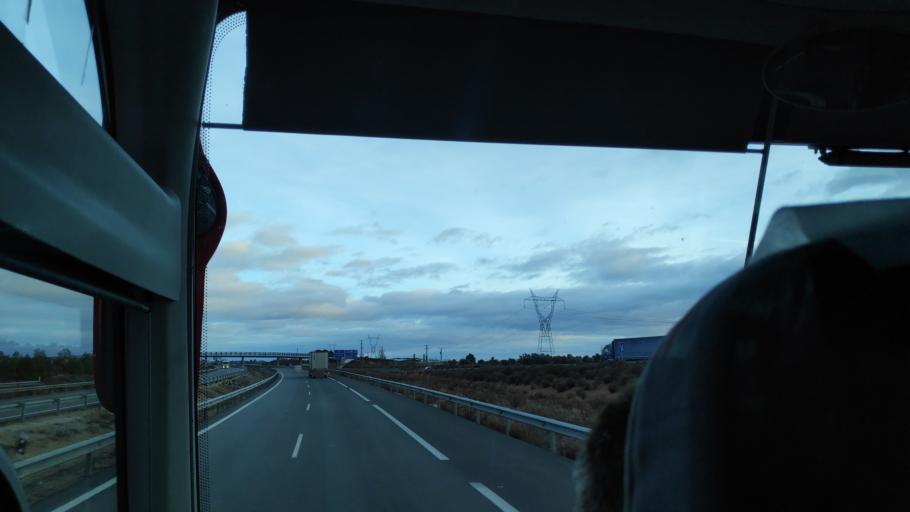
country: ES
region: Castille-La Mancha
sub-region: Provincia de Cuenca
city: Tarancon
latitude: 39.9991
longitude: -3.0211
